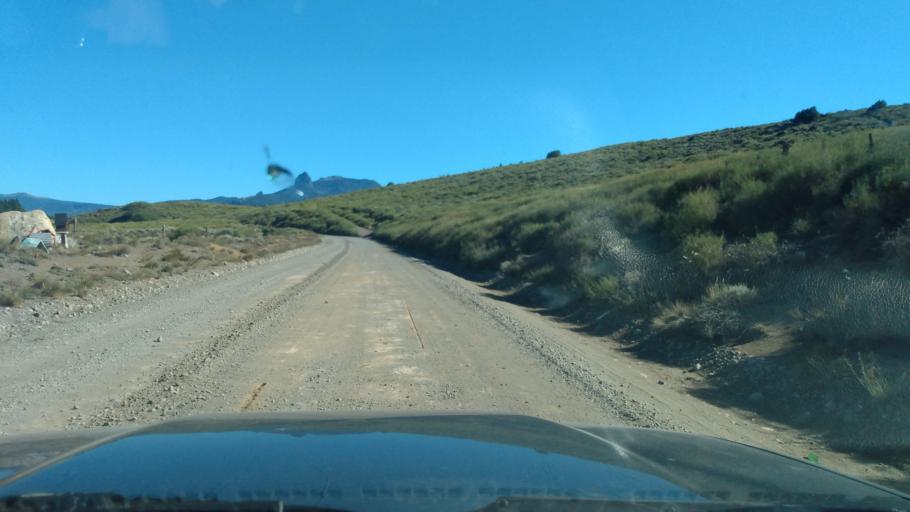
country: AR
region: Neuquen
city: Junin de los Andes
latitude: -39.8079
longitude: -71.2072
